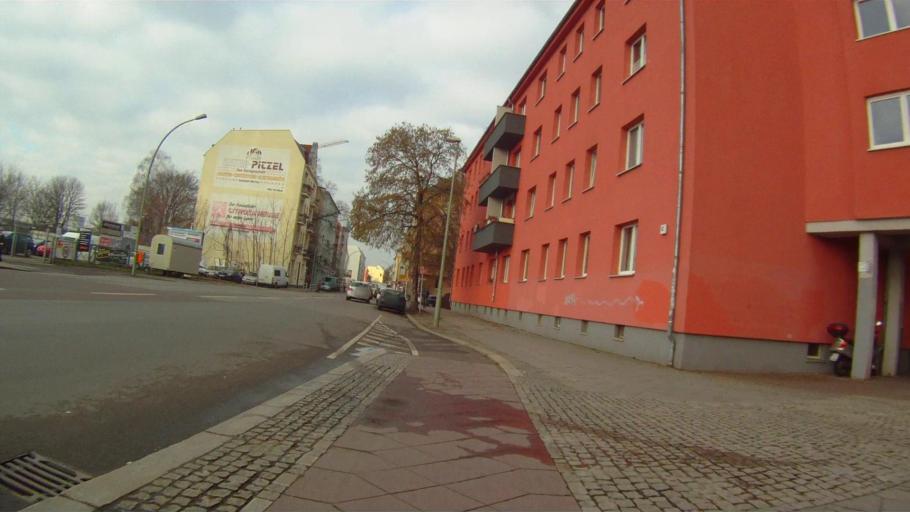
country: DE
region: Berlin
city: Rummelsburg
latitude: 52.5004
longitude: 13.4958
